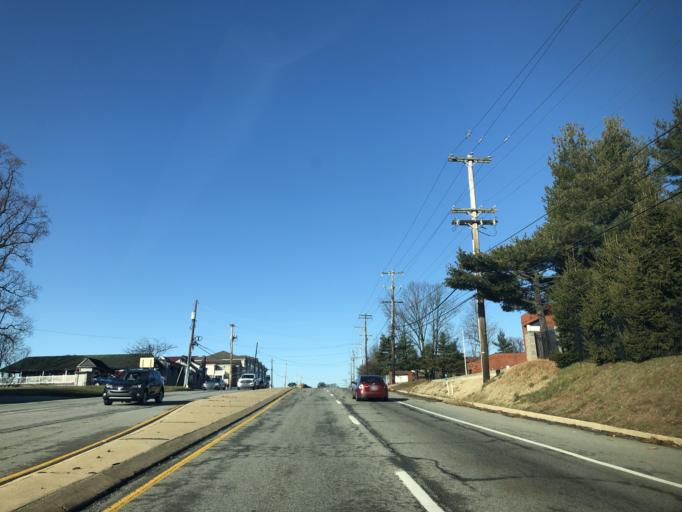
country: US
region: Pennsylvania
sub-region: Delaware County
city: Chester Heights
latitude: 39.8964
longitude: -75.4812
